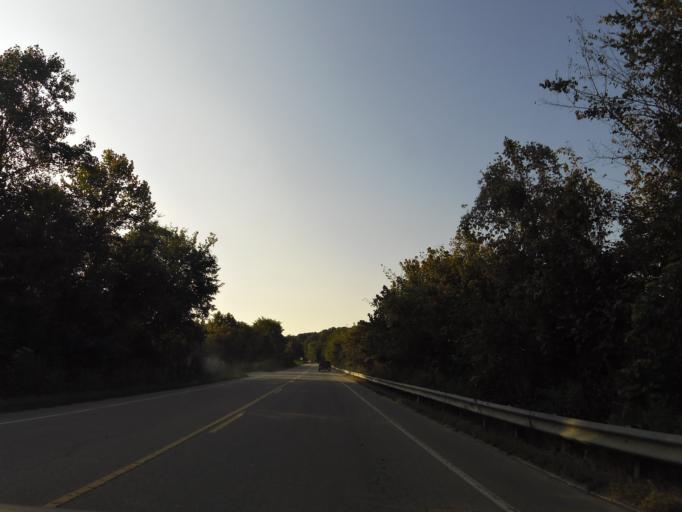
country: US
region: Tennessee
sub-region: Knox County
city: Mascot
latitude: 36.0671
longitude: -83.7374
